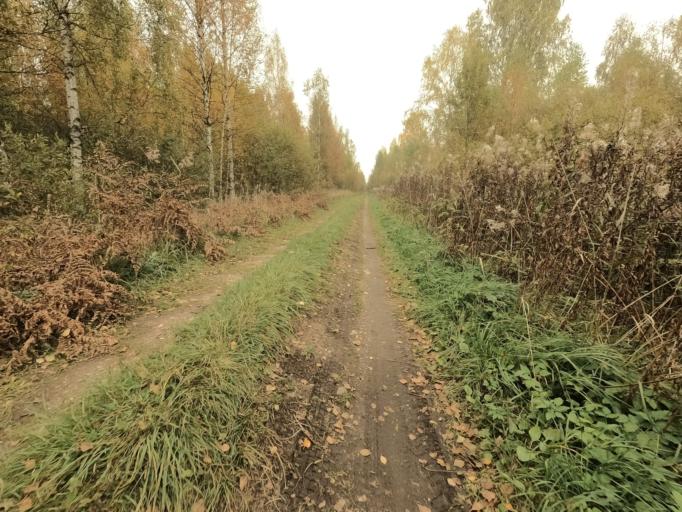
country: RU
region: Novgorod
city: Pankovka
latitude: 58.8895
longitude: 30.9489
